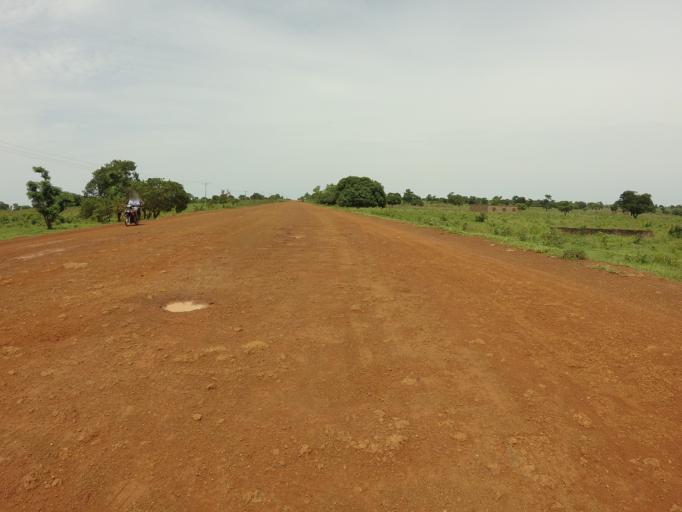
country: GH
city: Kpandae
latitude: 8.8346
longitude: 0.0609
